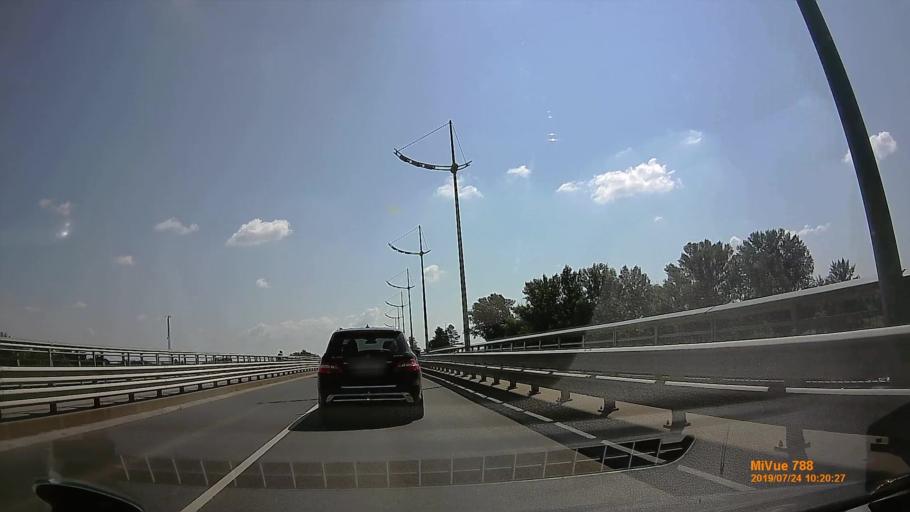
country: HU
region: Szabolcs-Szatmar-Bereg
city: Vasarosnameny
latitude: 48.1262
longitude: 22.3390
